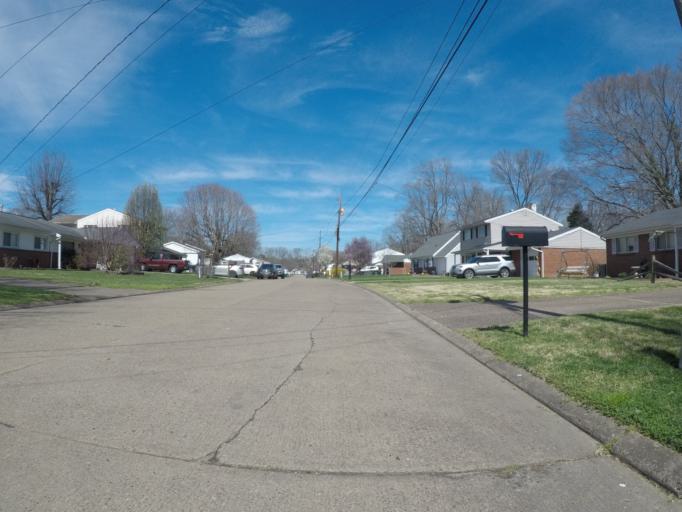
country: US
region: West Virginia
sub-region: Cabell County
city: Pea Ridge
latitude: 38.4005
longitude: -82.3138
